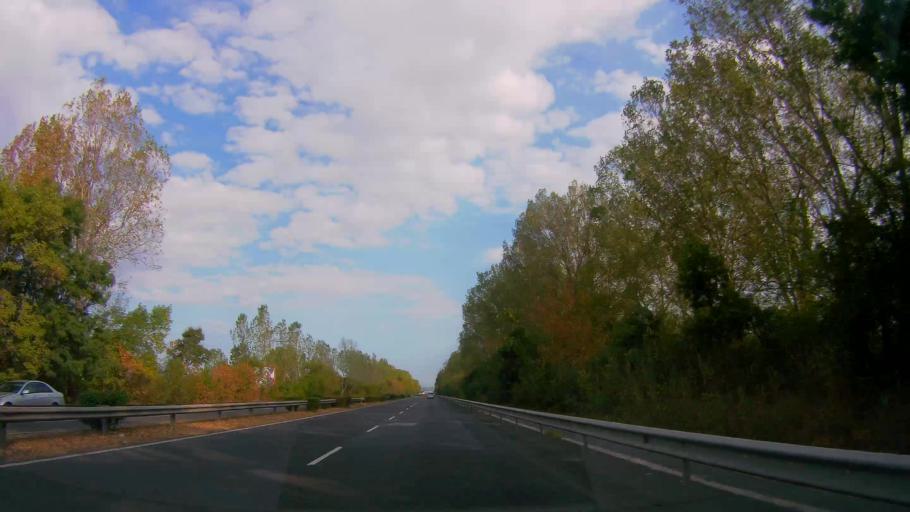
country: BG
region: Burgas
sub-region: Obshtina Burgas
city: Burgas
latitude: 42.4612
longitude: 27.4395
